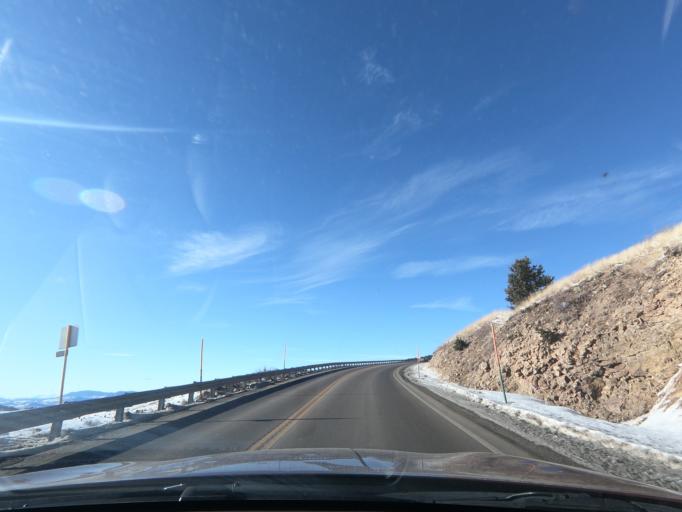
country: US
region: Colorado
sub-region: Teller County
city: Cripple Creek
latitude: 38.7551
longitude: -105.1621
